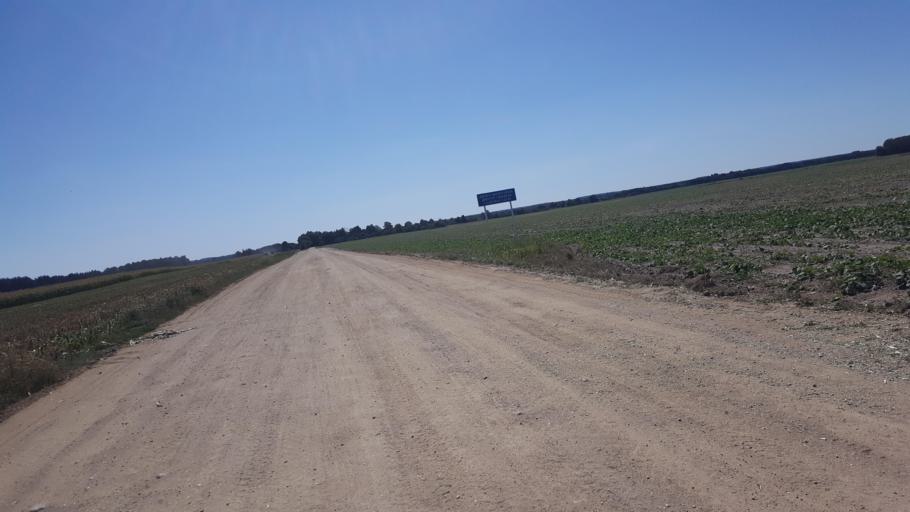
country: PL
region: Lublin Voivodeship
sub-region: Powiat bialski
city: Rokitno
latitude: 52.2226
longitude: 23.3988
